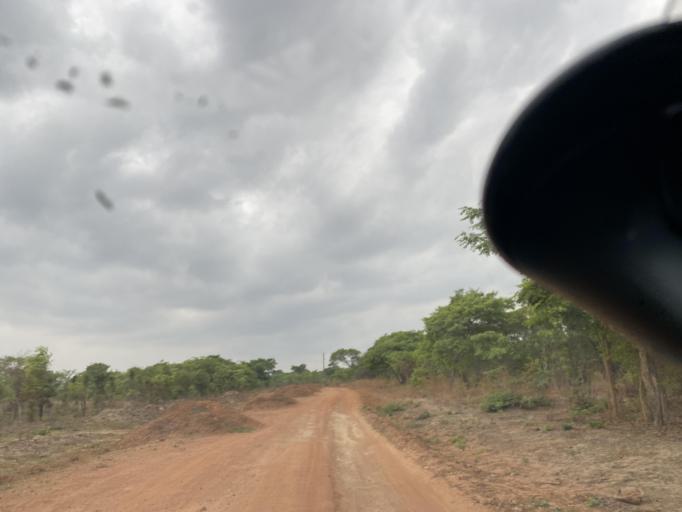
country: ZM
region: Lusaka
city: Chongwe
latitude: -15.2304
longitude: 28.7251
